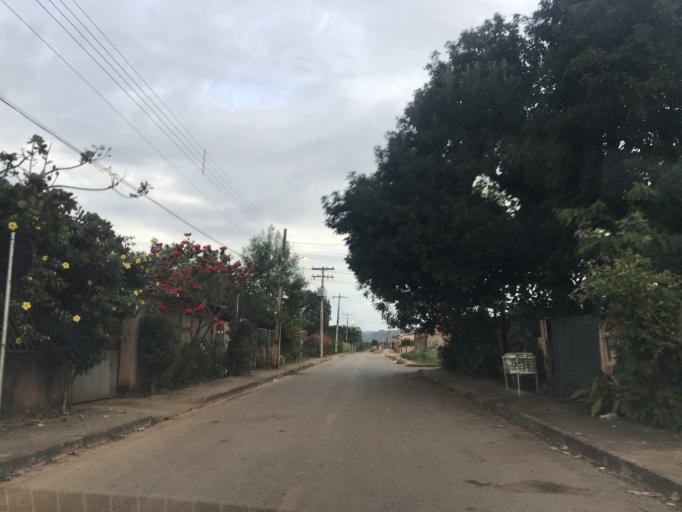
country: BR
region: Goias
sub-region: Padre Bernardo
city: Padre Bernardo
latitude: -15.3607
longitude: -48.2270
